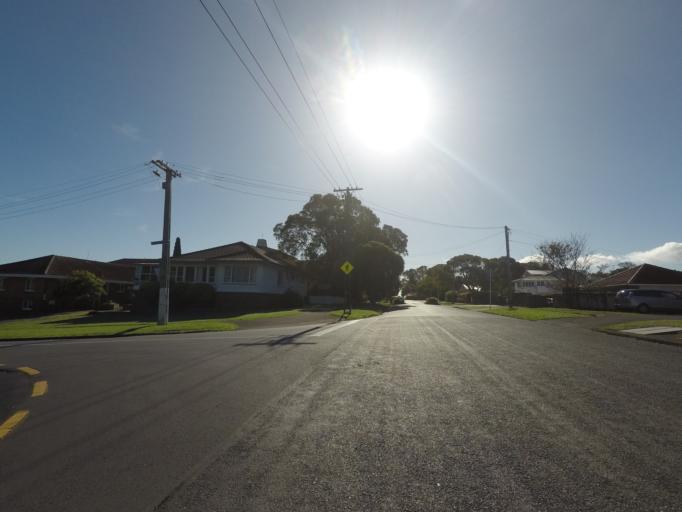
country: NZ
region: Auckland
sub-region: Auckland
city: Rosebank
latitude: -36.8896
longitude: 174.7130
